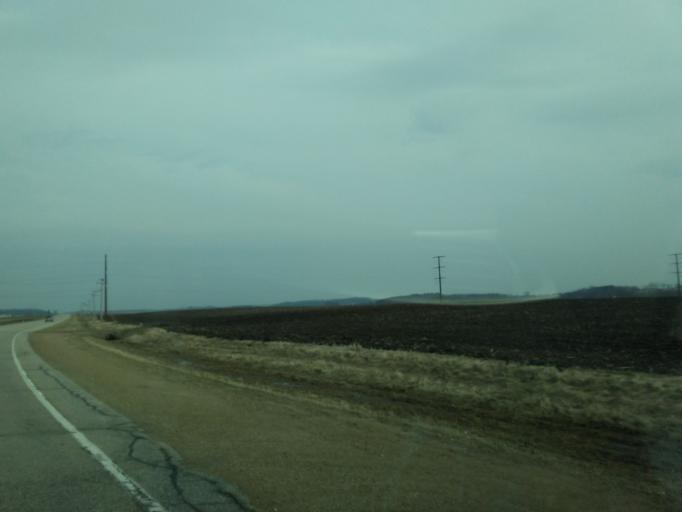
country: US
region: Wisconsin
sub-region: Columbia County
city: Lodi
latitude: 43.2539
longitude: -89.5210
